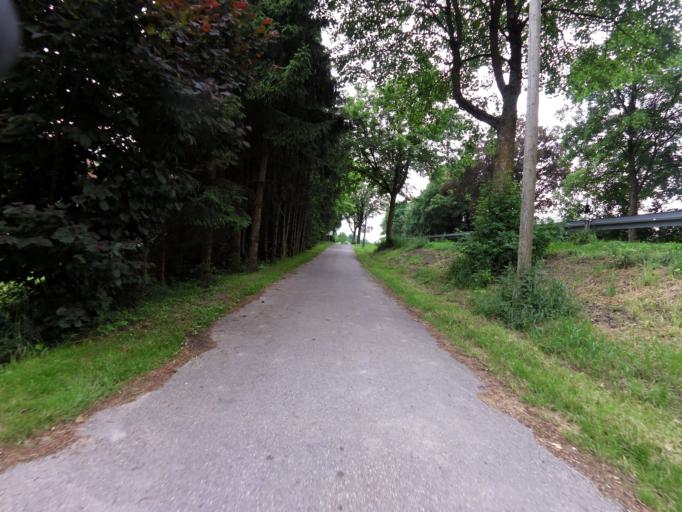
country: DE
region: Bavaria
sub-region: Upper Bavaria
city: Moosburg
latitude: 48.4511
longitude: 11.9054
